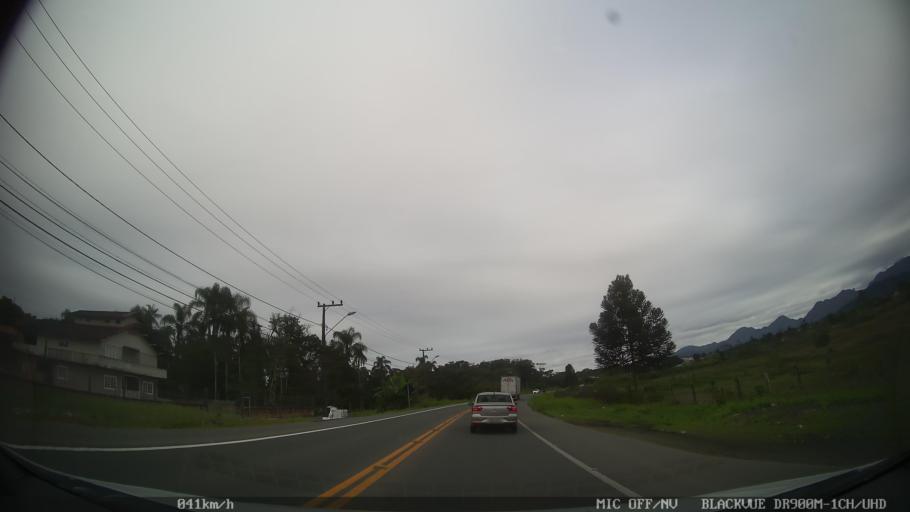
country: BR
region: Santa Catarina
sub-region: Joinville
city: Joinville
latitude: -26.3071
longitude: -48.9199
